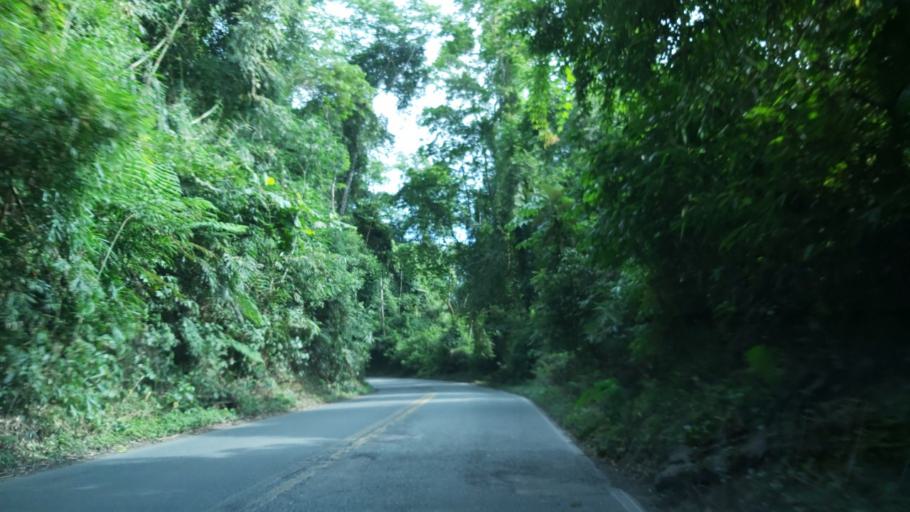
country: BR
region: Sao Paulo
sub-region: Juquia
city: Juquia
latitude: -24.0959
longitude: -47.6149
